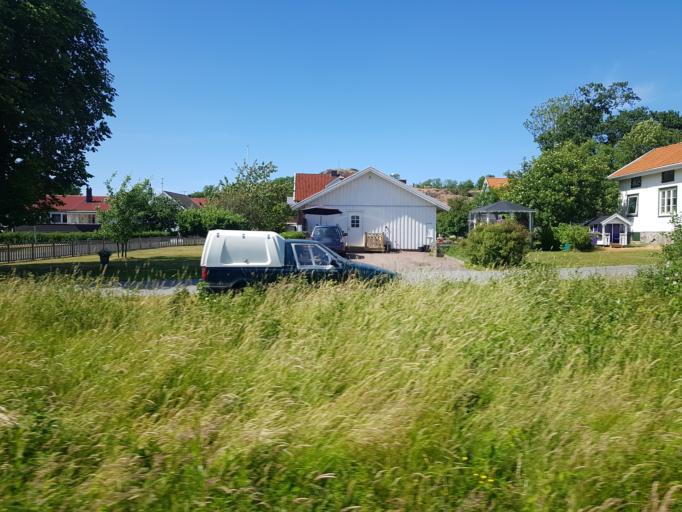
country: SE
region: Vaestra Goetaland
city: Ronnang
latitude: 57.9410
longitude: 11.5981
